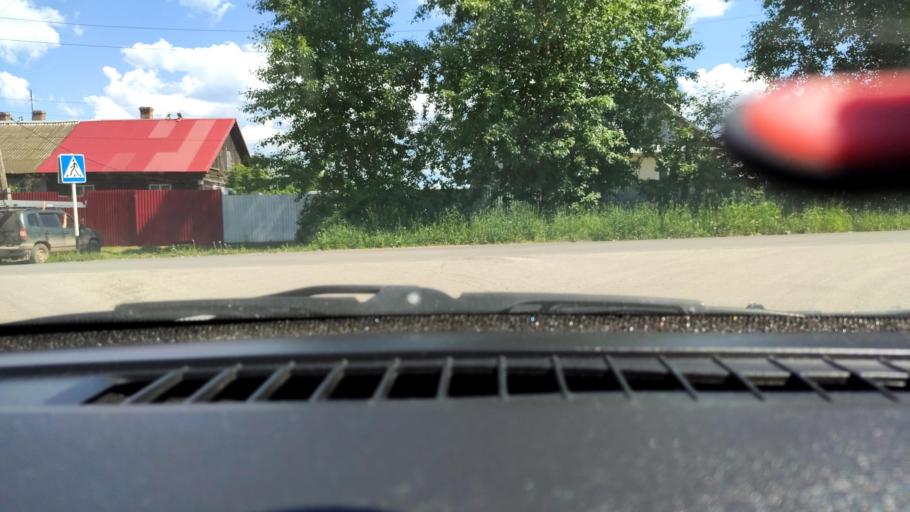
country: RU
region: Perm
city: Sylva
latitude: 58.0318
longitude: 56.7589
